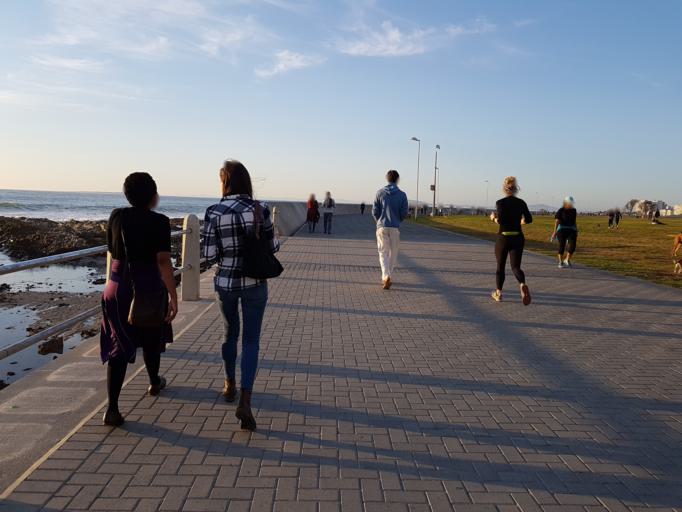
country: ZA
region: Western Cape
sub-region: City of Cape Town
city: Cape Town
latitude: -33.9119
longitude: 18.3882
